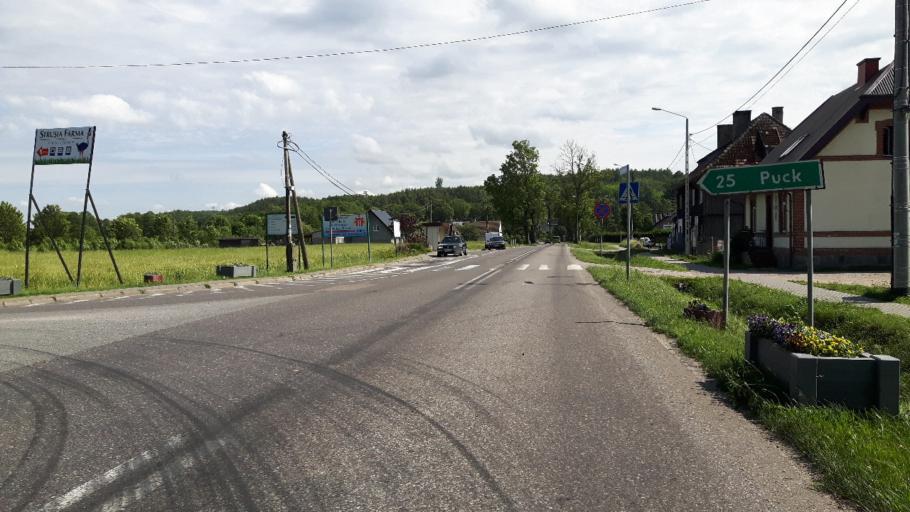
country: PL
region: Pomeranian Voivodeship
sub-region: Powiat wejherowski
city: Orle
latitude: 54.6527
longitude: 18.0999
